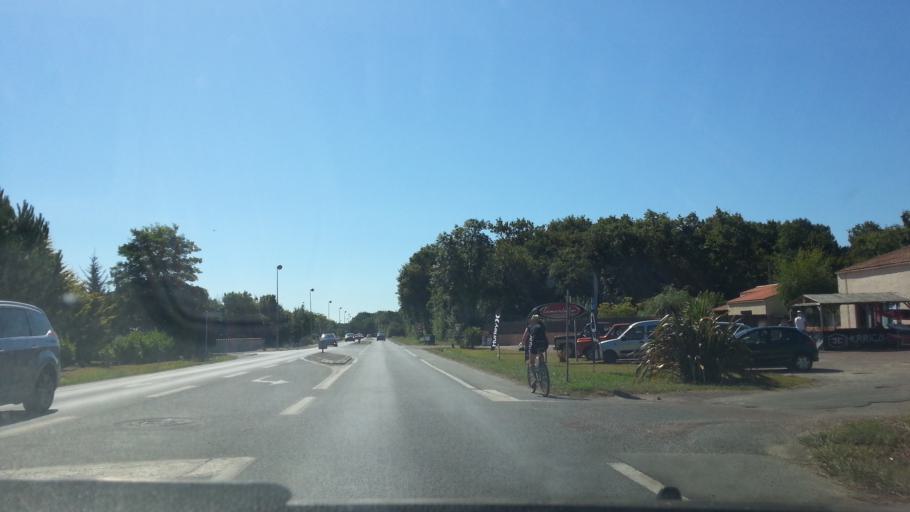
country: FR
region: Poitou-Charentes
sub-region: Departement de la Charente-Maritime
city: Dolus-d'Oleron
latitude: 45.9163
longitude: -1.2738
